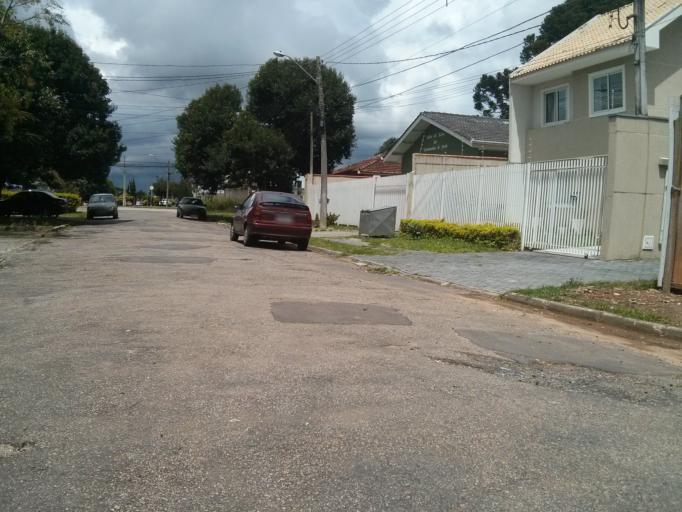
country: BR
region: Parana
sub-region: Sao Jose Dos Pinhais
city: Sao Jose dos Pinhais
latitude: -25.5240
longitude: -49.2306
